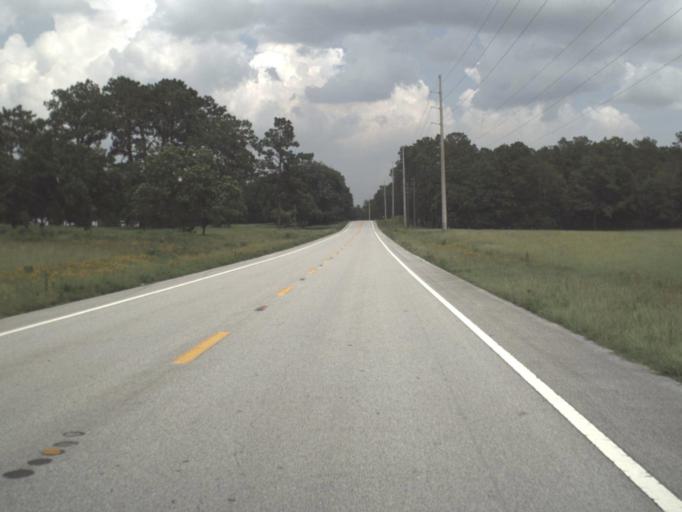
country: US
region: Florida
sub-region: Madison County
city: Madison
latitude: 30.4722
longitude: -83.2773
